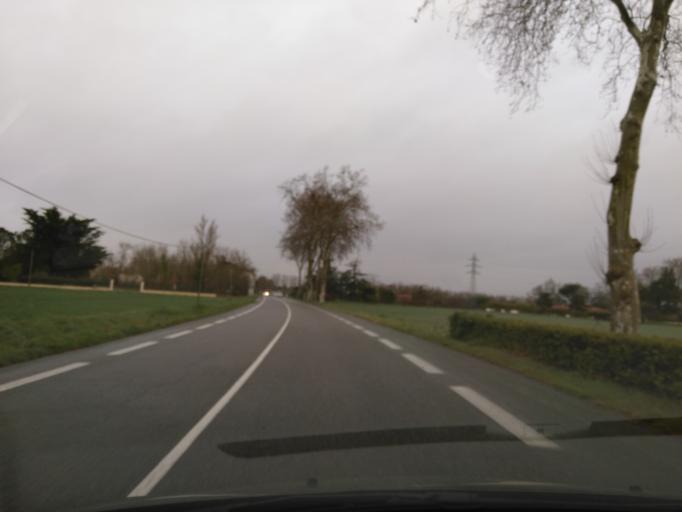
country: FR
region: Midi-Pyrenees
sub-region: Departement de la Haute-Garonne
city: Carbonne
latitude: 43.2858
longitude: 1.2169
